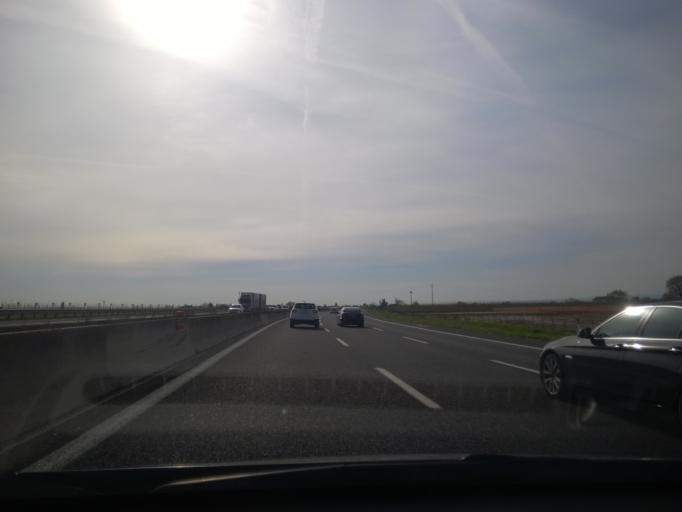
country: IT
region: Emilia-Romagna
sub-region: Forli-Cesena
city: Forlimpopoli
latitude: 44.2411
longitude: 12.1271
